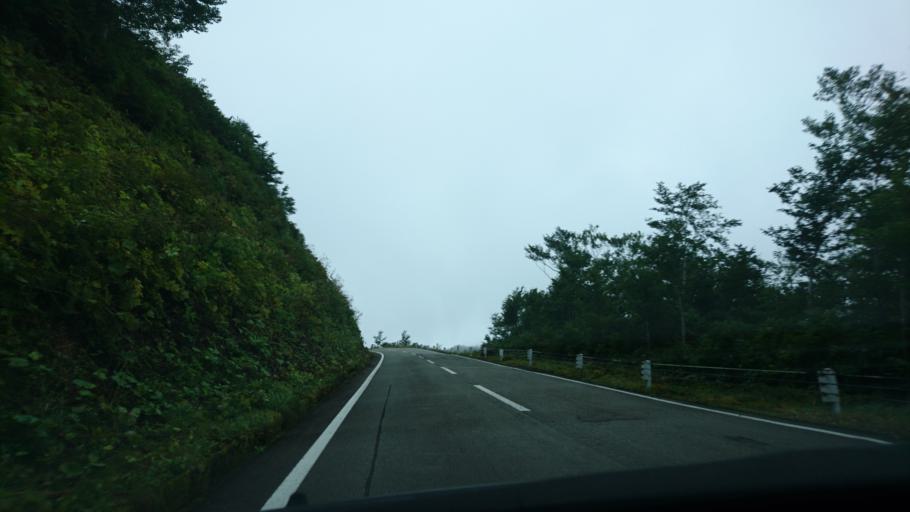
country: JP
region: Akita
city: Yuzawa
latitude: 38.9790
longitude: 140.7555
